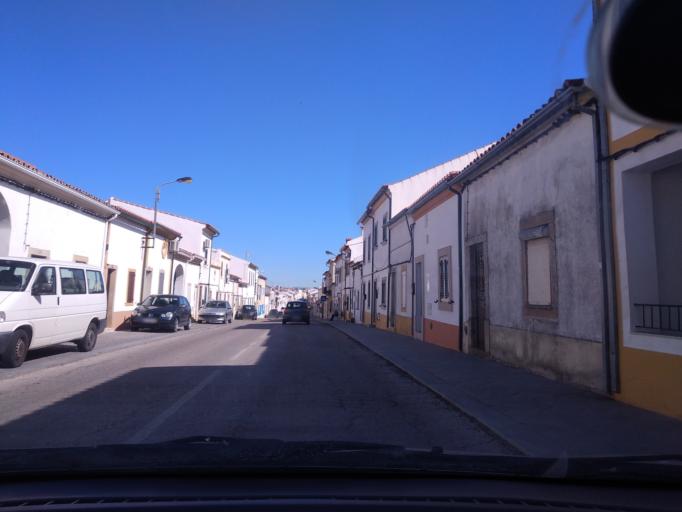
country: PT
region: Portalegre
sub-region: Nisa
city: Nisa
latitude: 39.5098
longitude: -7.6462
